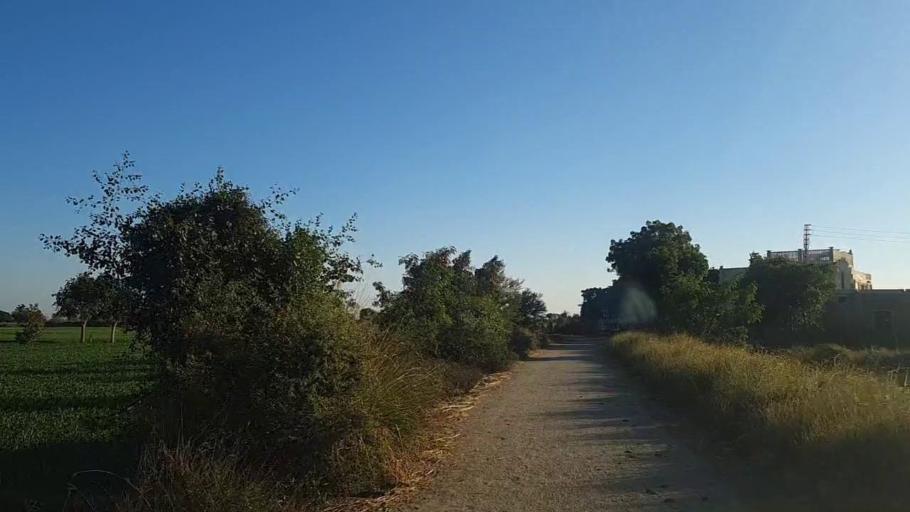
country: PK
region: Sindh
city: Sanghar
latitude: 26.1356
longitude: 68.9430
